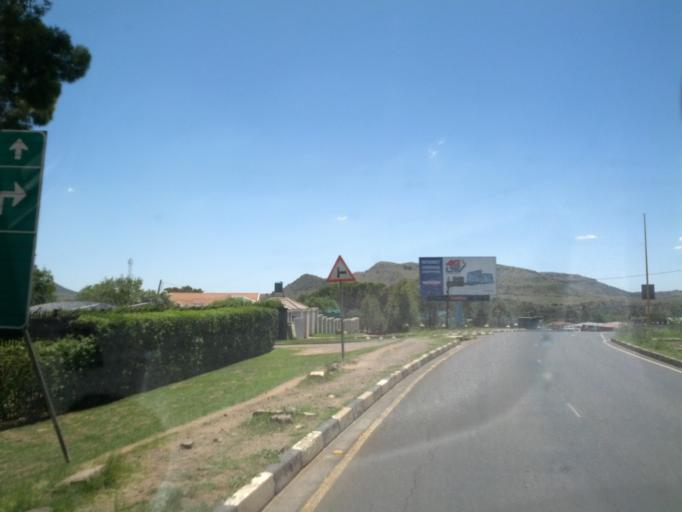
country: LS
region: Maseru
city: Maseru
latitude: -29.3059
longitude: 27.4681
